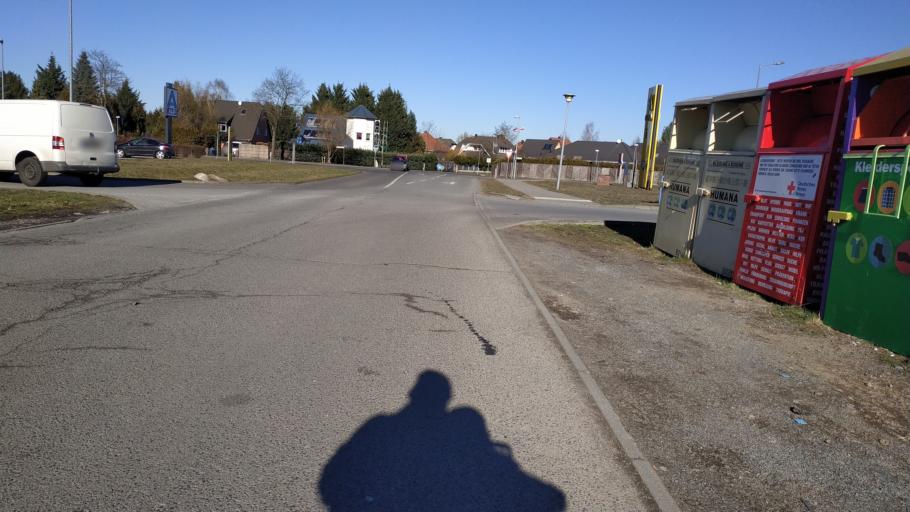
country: DE
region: Brandenburg
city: Petershagen
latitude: 52.5317
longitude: 13.8070
